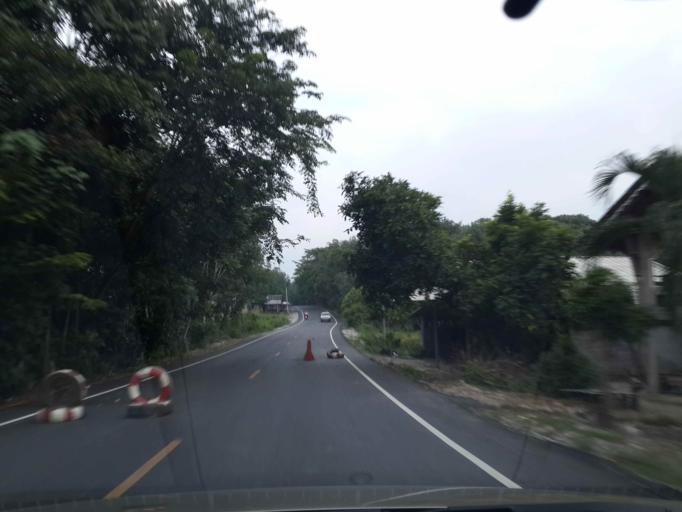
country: TH
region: Narathiwat
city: Rueso
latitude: 6.3527
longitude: 101.4721
